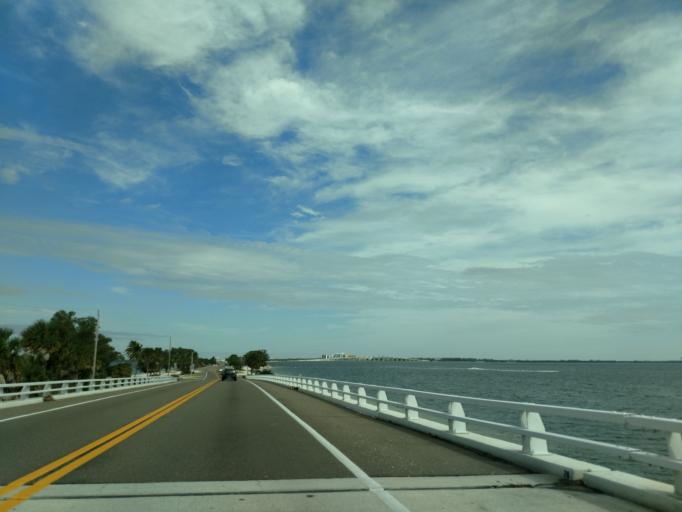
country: US
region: Florida
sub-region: Lee County
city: Sanibel
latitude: 26.4636
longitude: -82.0317
